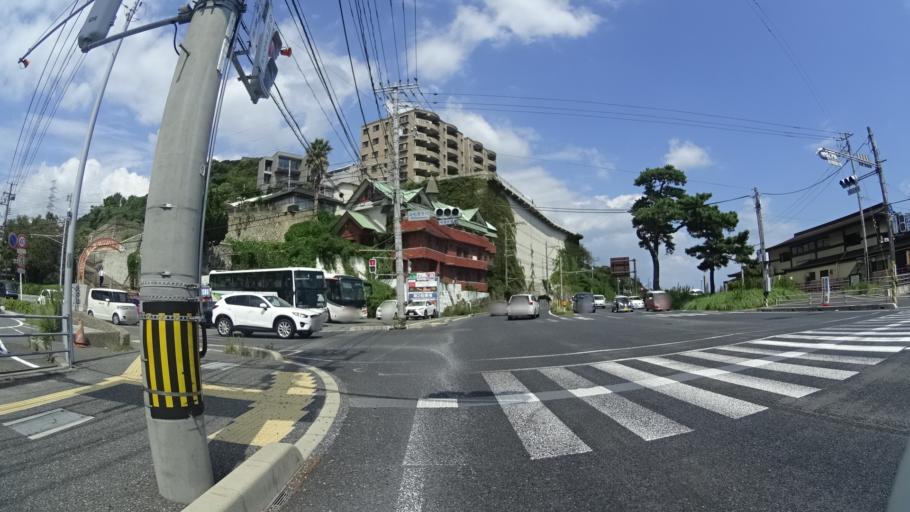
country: JP
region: Yamaguchi
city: Shimonoseki
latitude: 33.9663
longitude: 130.9560
